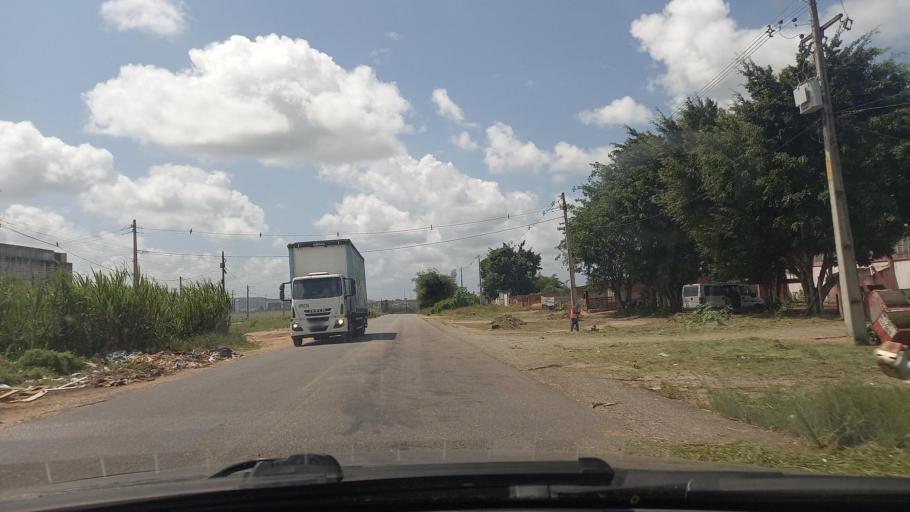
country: BR
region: Pernambuco
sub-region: Goiana
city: Goiana
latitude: -7.5579
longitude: -35.0277
